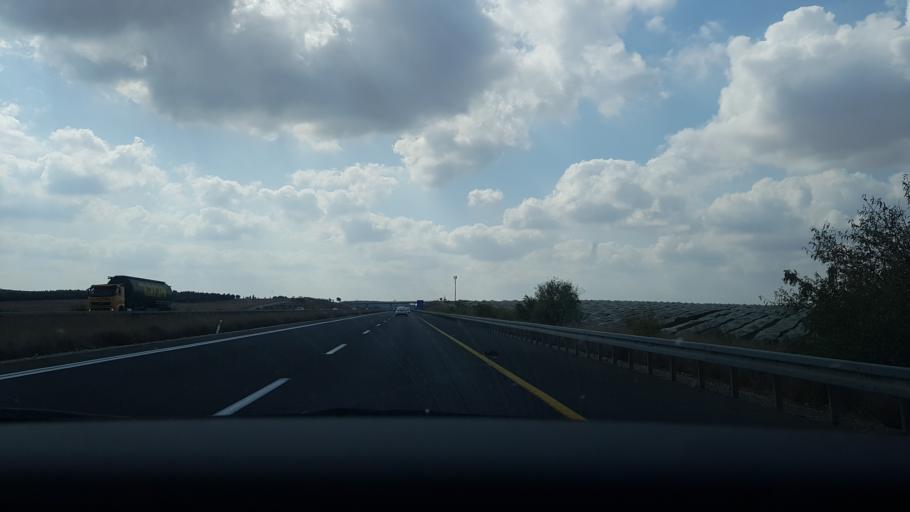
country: IL
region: Southern District
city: Qiryat Gat
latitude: 31.6211
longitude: 34.8145
